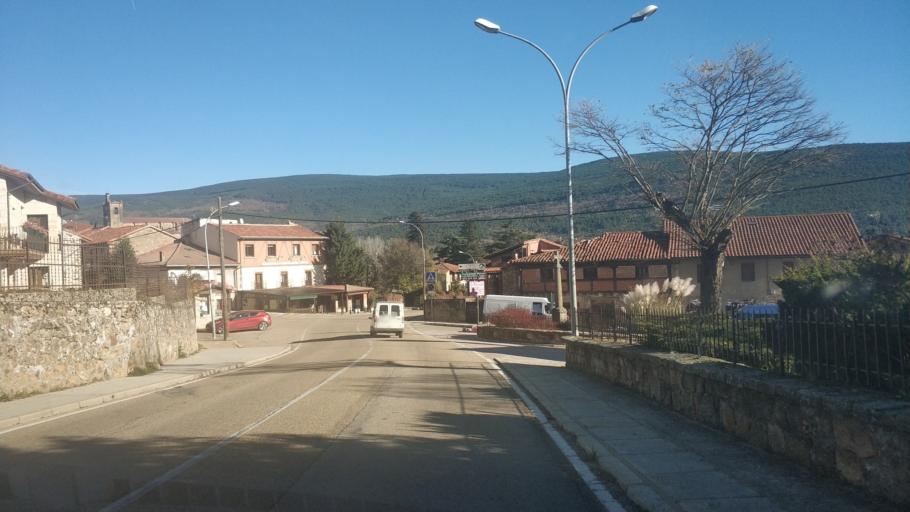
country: ES
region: Castille and Leon
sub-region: Provincia de Soria
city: Vinuesa
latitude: 41.9084
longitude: -2.7641
